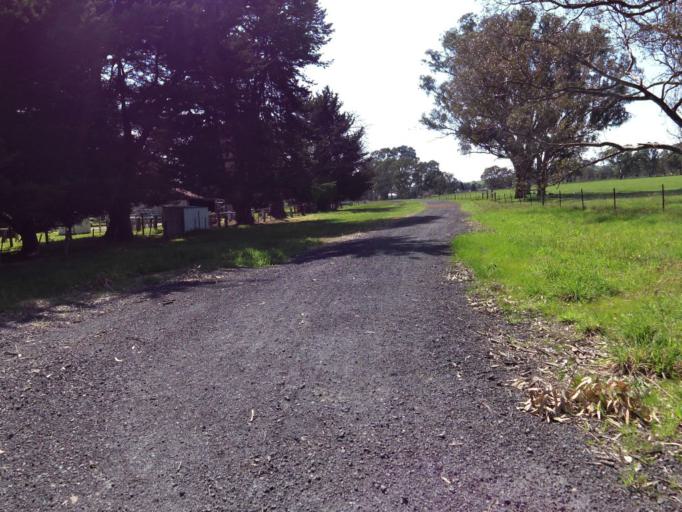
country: AU
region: Victoria
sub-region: Murrindindi
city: Alexandra
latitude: -37.1108
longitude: 145.6109
